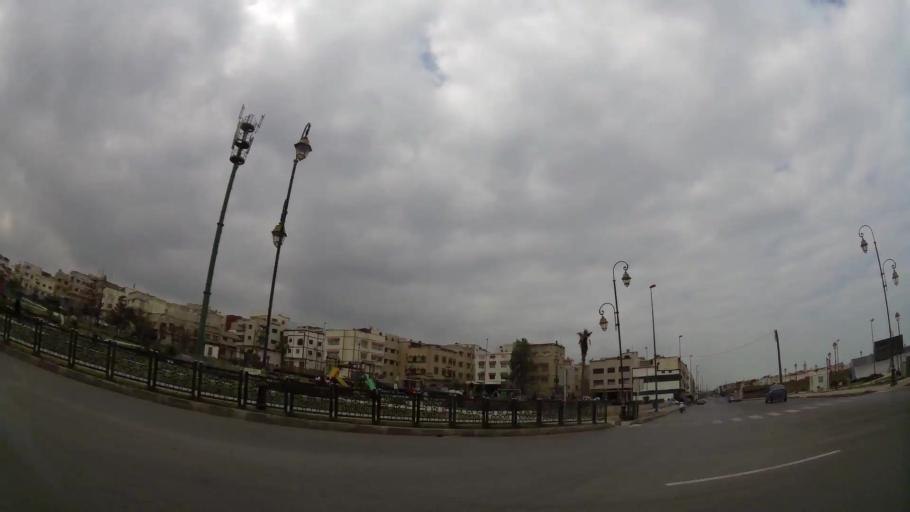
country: MA
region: Rabat-Sale-Zemmour-Zaer
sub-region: Rabat
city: Rabat
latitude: 33.9900
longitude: -6.8823
